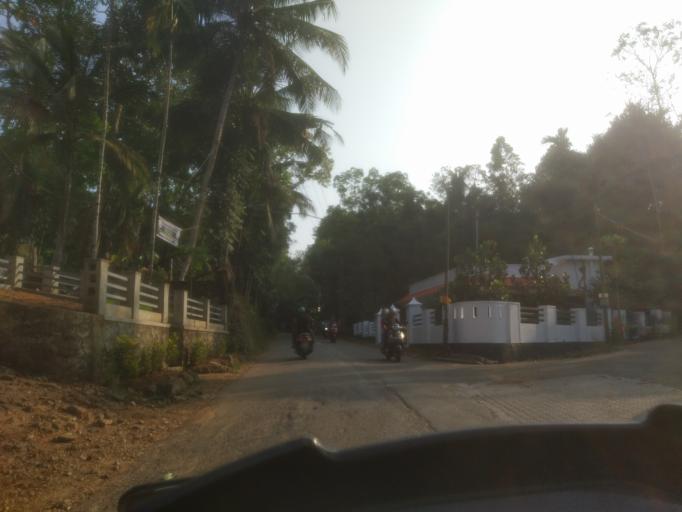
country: IN
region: Kerala
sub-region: Ernakulam
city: Piravam
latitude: 9.8110
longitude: 76.4969
